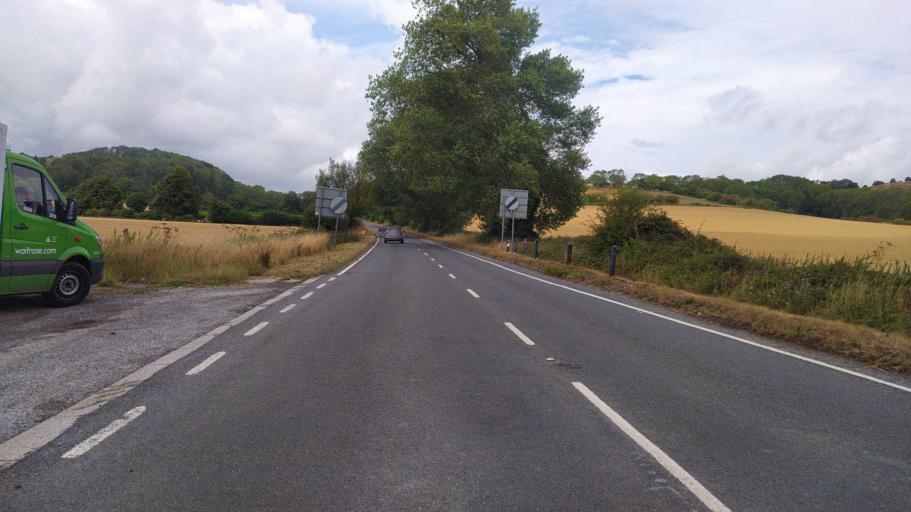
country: GB
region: England
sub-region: Hampshire
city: Petersfield
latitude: 50.9707
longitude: -0.8858
